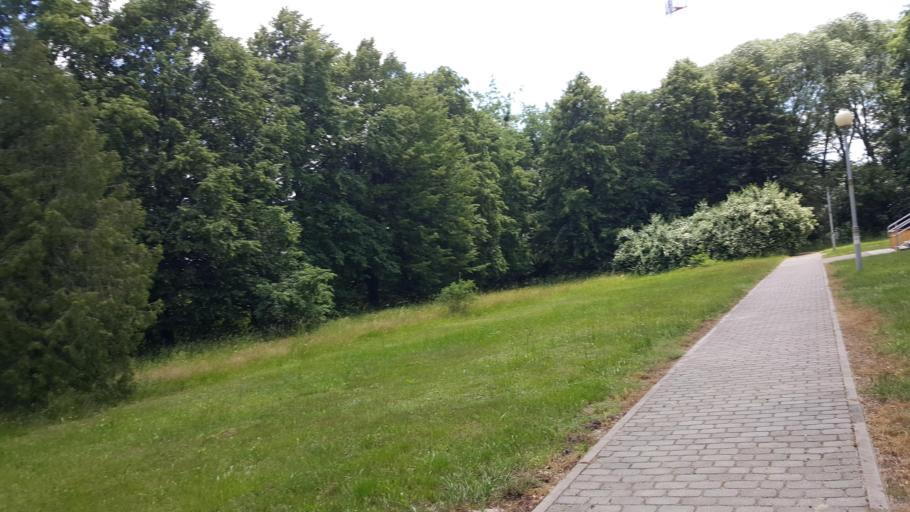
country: BY
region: Brest
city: Kamyanyuki
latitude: 52.5570
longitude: 23.7983
